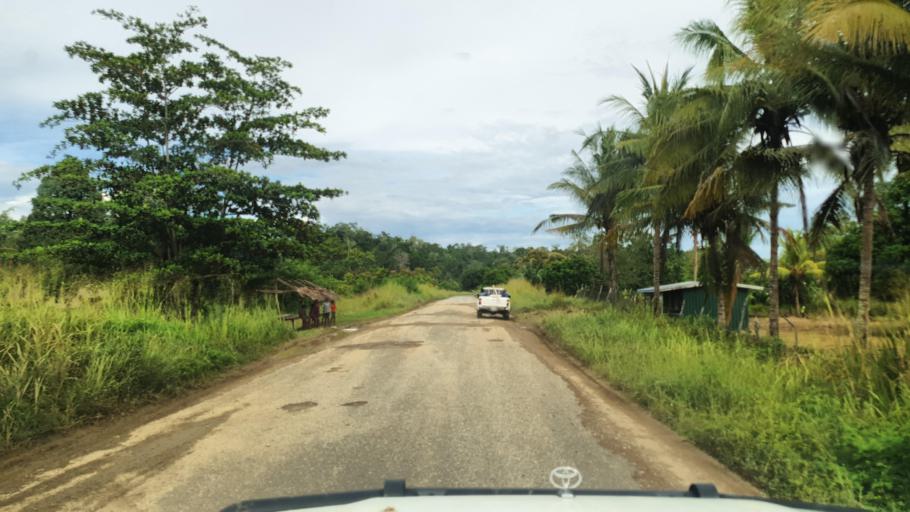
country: PG
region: Gulf
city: Kerema
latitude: -8.3377
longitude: 146.3258
